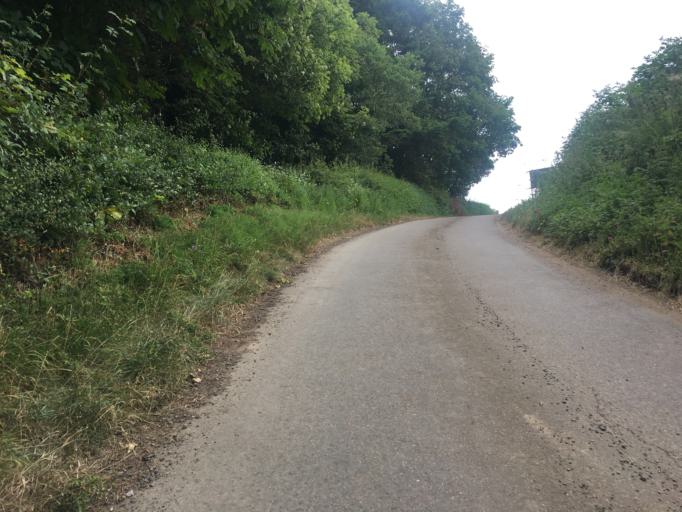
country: GB
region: England
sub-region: Northumberland
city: Belford
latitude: 55.6013
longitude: -1.7778
